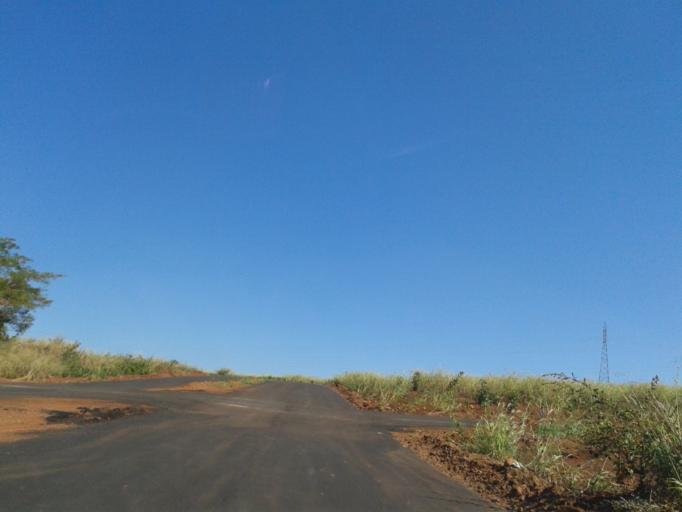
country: BR
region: Minas Gerais
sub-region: Capinopolis
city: Capinopolis
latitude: -18.5354
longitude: -49.4989
